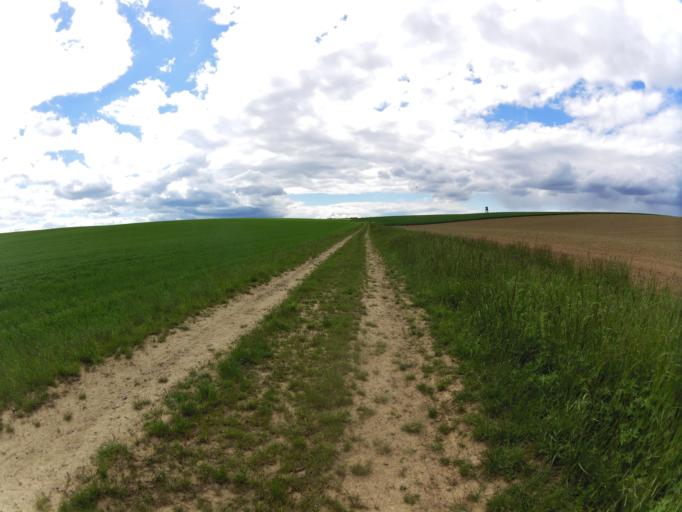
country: DE
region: Bavaria
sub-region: Regierungsbezirk Unterfranken
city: Volkach
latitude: 49.8807
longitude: 10.2402
